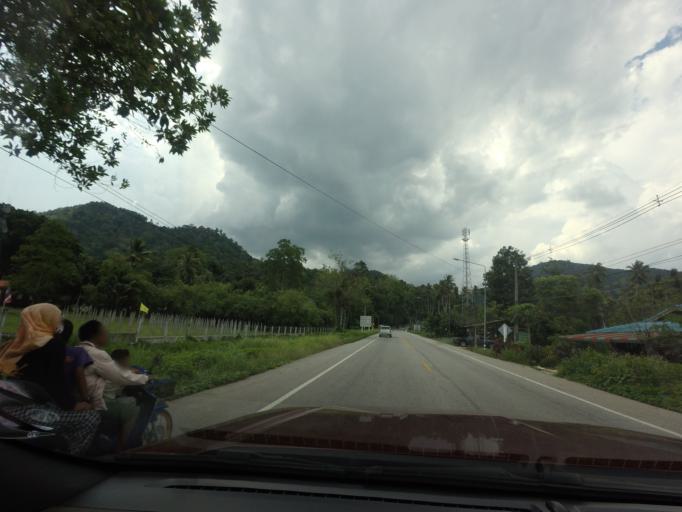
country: TH
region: Yala
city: Than To
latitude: 6.1967
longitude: 101.1735
